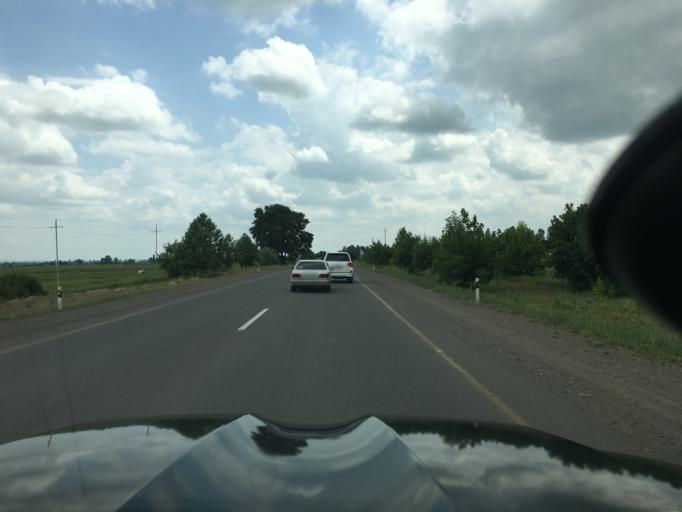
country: AZ
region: Tovuz
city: Tovuz
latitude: 40.9631
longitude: 45.7129
